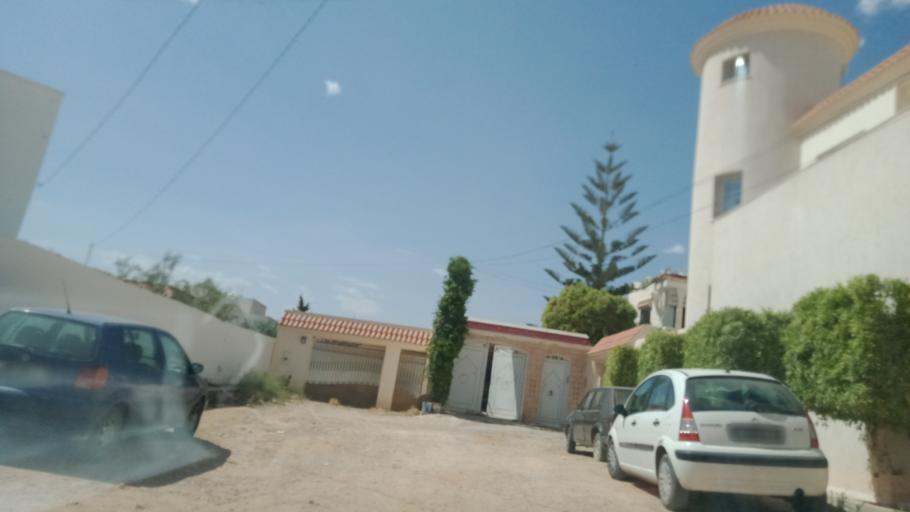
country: TN
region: Safaqis
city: Al Qarmadah
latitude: 34.8030
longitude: 10.7554
